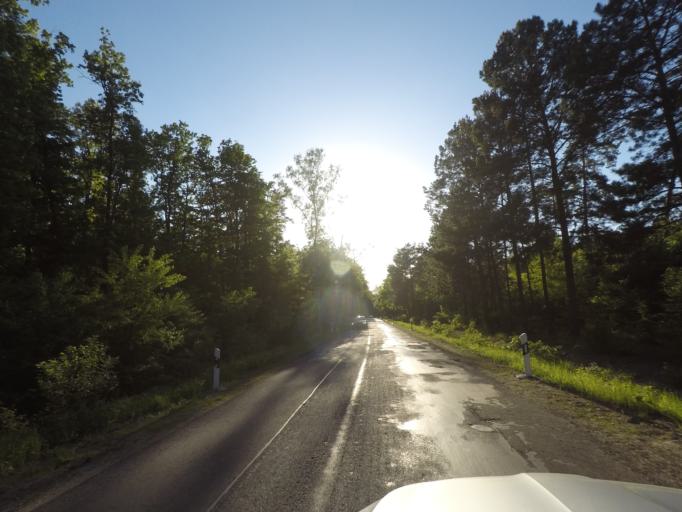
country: DE
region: Brandenburg
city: Bad Freienwalde
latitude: 52.8160
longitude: 14.0265
